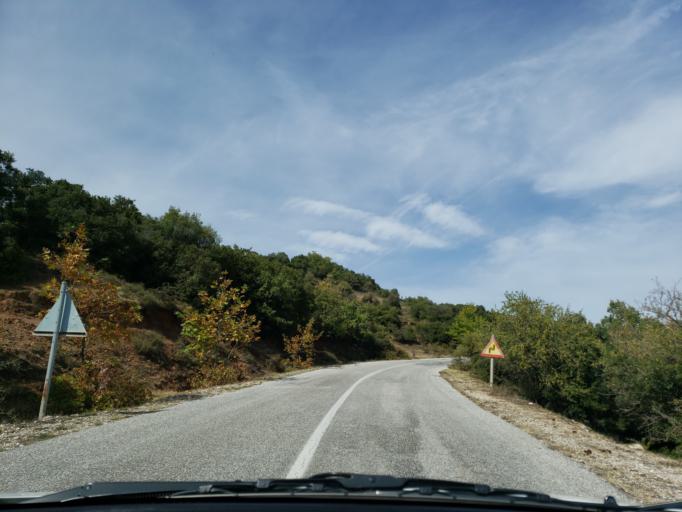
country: GR
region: Thessaly
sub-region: Trikala
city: Kalampaka
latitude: 39.7243
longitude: 21.6497
